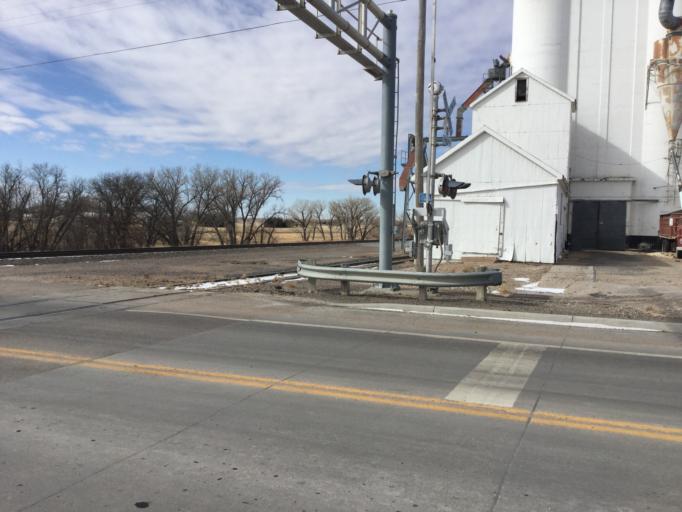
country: US
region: Kansas
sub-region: Wallace County
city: Sharon Springs
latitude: 38.8945
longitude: -101.7517
